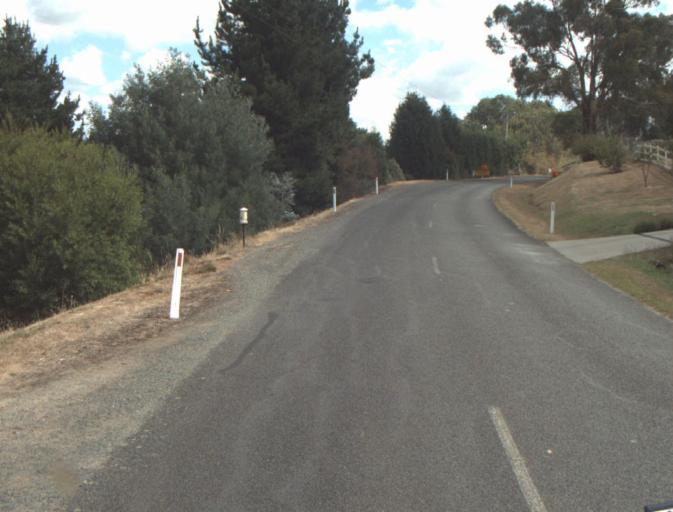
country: AU
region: Tasmania
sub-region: Launceston
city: Mayfield
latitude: -41.3142
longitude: 147.0401
